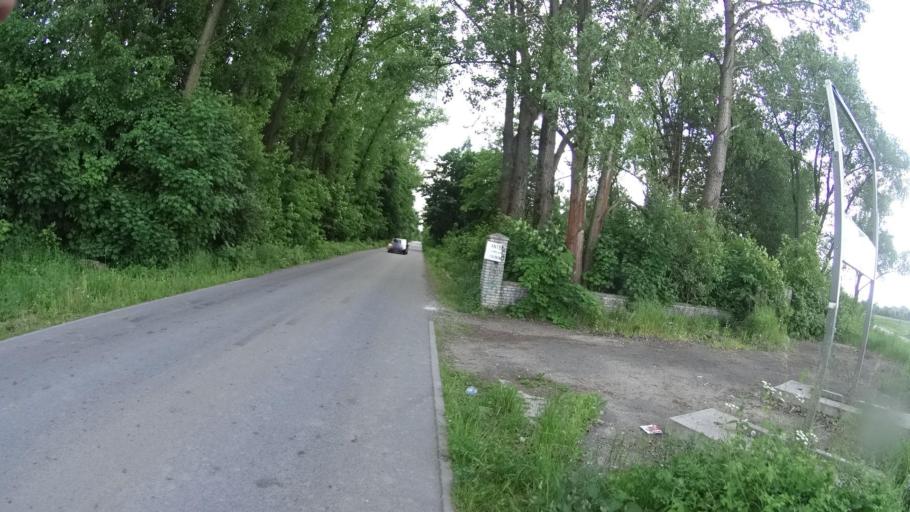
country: PL
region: Masovian Voivodeship
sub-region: Powiat pruszkowski
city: Nadarzyn
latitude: 52.0765
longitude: 20.8179
